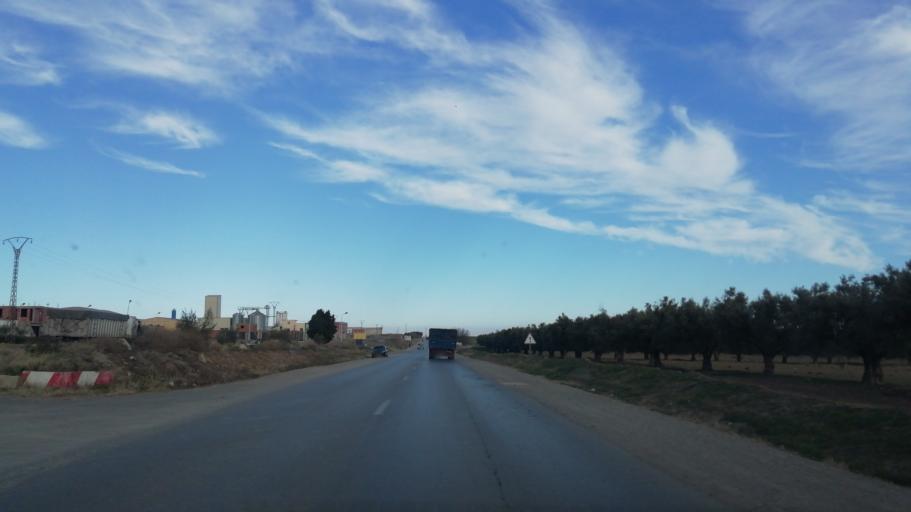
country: DZ
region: Sidi Bel Abbes
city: Sfizef
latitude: 35.2422
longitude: -0.2248
